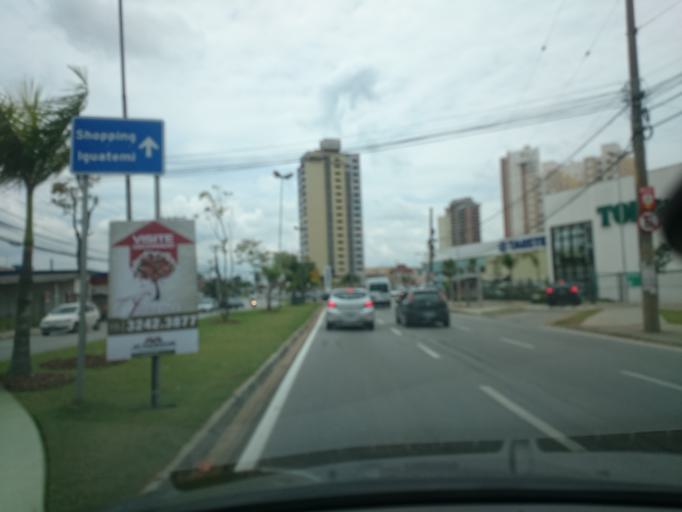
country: BR
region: Sao Paulo
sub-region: Votorantim
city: Votorantim
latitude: -23.5367
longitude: -47.4657
